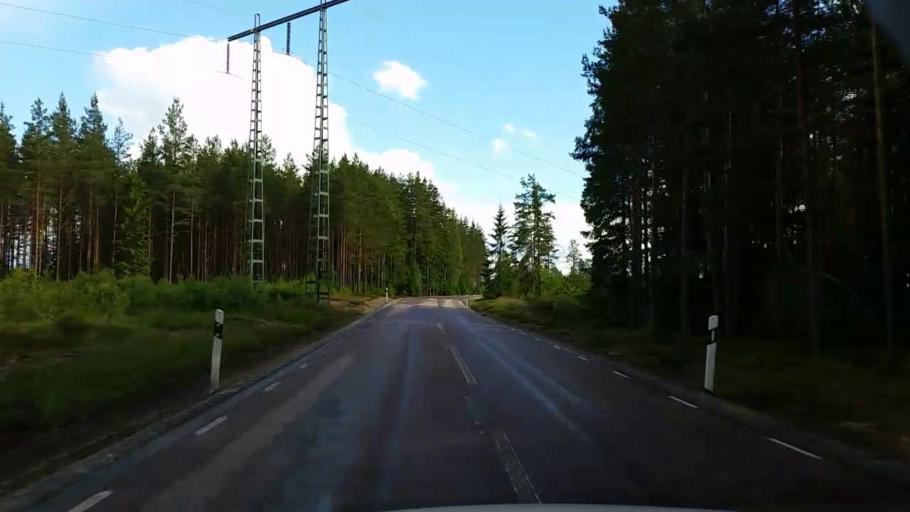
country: SE
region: Vaestmanland
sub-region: Fagersta Kommun
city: Fagersta
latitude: 59.8974
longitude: 15.8203
